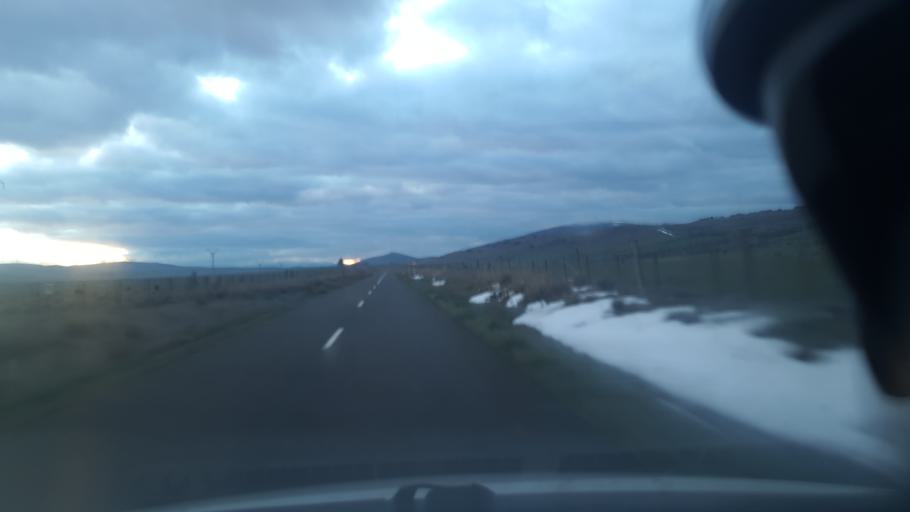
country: ES
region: Castille and Leon
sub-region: Provincia de Segovia
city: Villacastin
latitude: 40.7034
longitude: -4.3646
